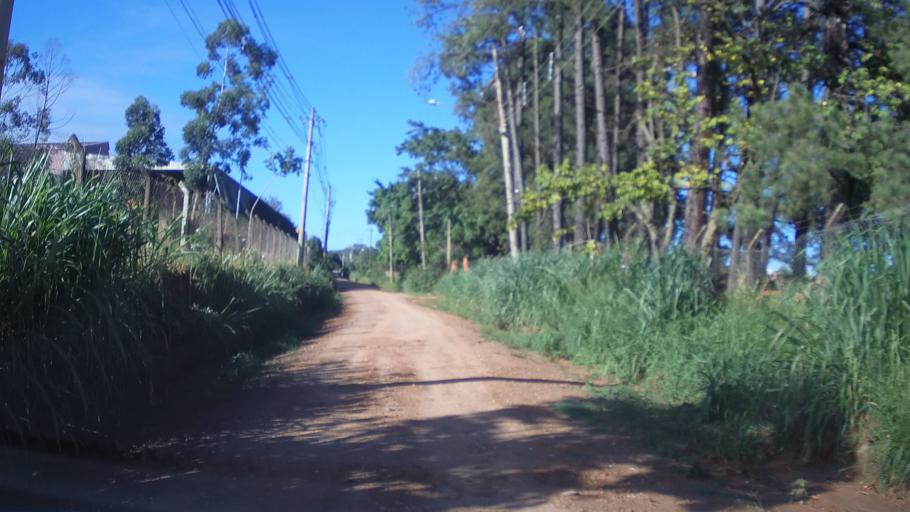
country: BR
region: Sao Paulo
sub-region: Itupeva
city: Itupeva
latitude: -23.1847
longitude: -46.9801
